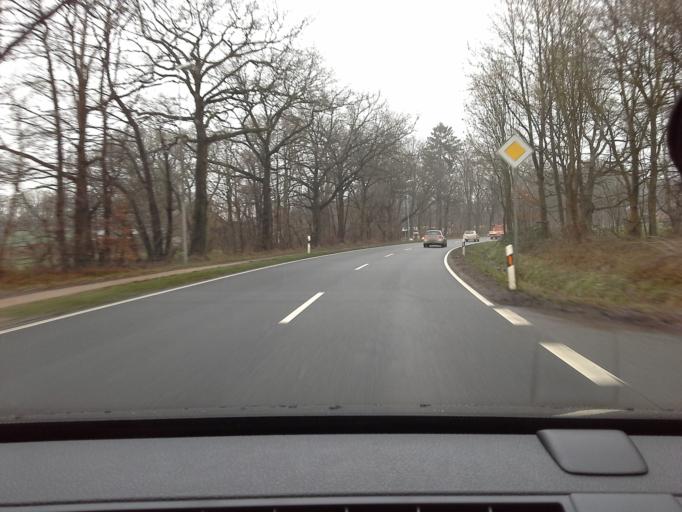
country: DE
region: Schleswig-Holstein
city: Ellerau
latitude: 53.7454
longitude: 9.9109
